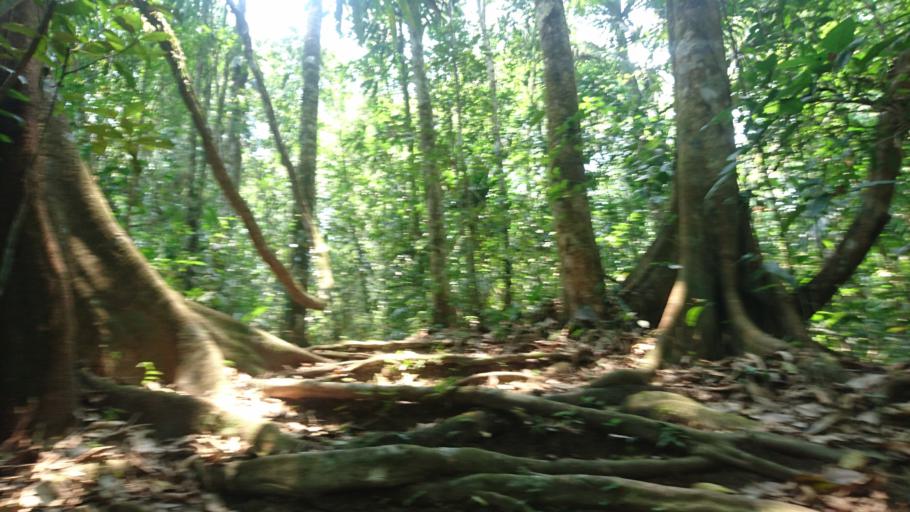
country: MX
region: Chiapas
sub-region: Marques de Comillas
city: Zamora Pico de Oro
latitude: 16.2478
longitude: -90.8314
